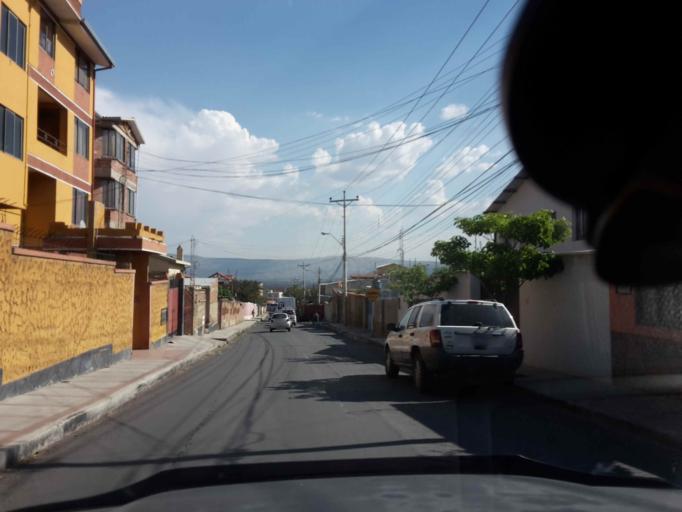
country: BO
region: Cochabamba
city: Cochabamba
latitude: -17.3499
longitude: -66.1889
